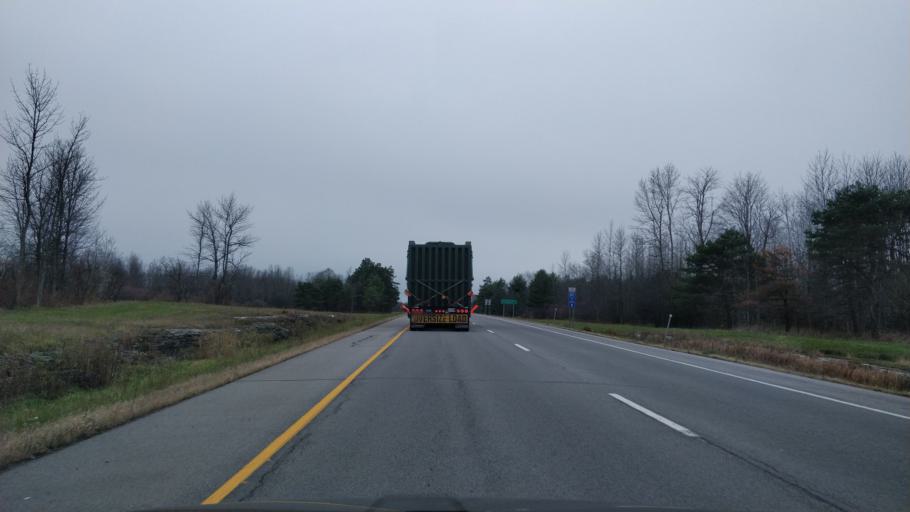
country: CA
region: Ontario
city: Brockville
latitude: 44.5768
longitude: -75.6432
